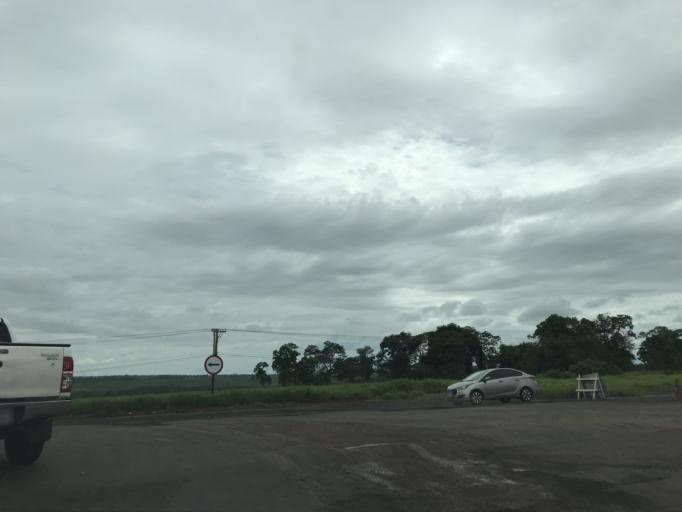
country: BR
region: Sao Paulo
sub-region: Nova Granada
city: Nova Granada
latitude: -20.3260
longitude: -49.2101
